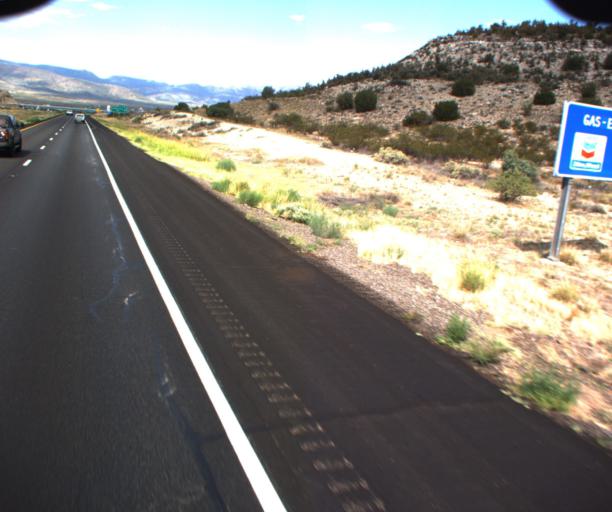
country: US
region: Arizona
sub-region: Yavapai County
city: Camp Verde
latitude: 34.6135
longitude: -111.8542
